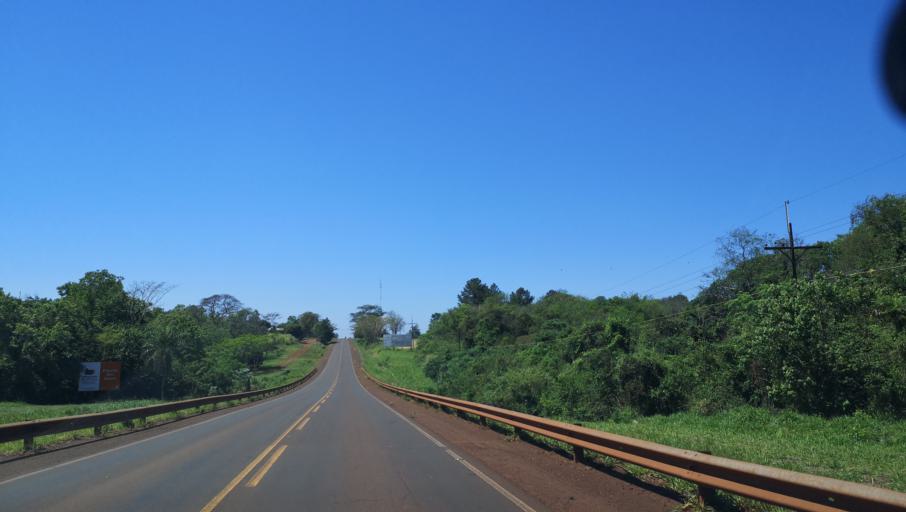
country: PY
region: Itapua
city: San Juan del Parana
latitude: -27.2591
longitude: -55.9670
